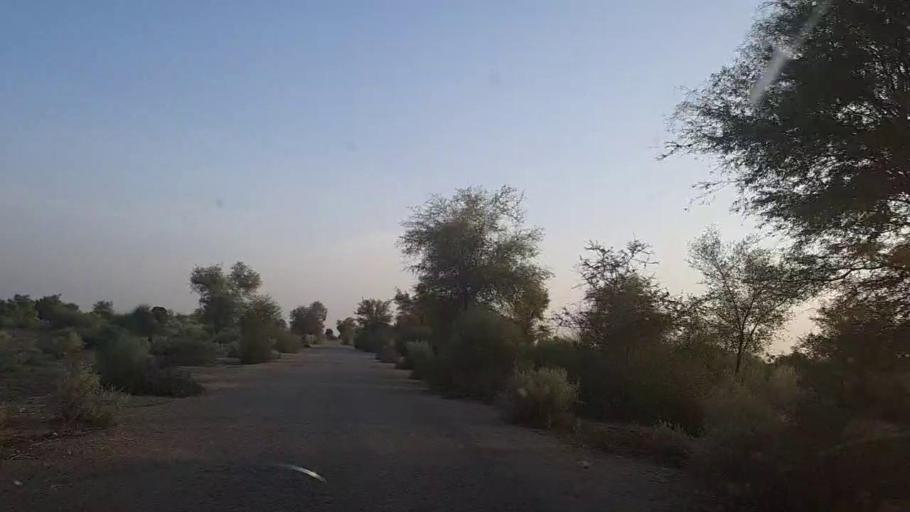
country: PK
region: Sindh
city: Khanpur
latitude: 27.6055
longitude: 69.4343
